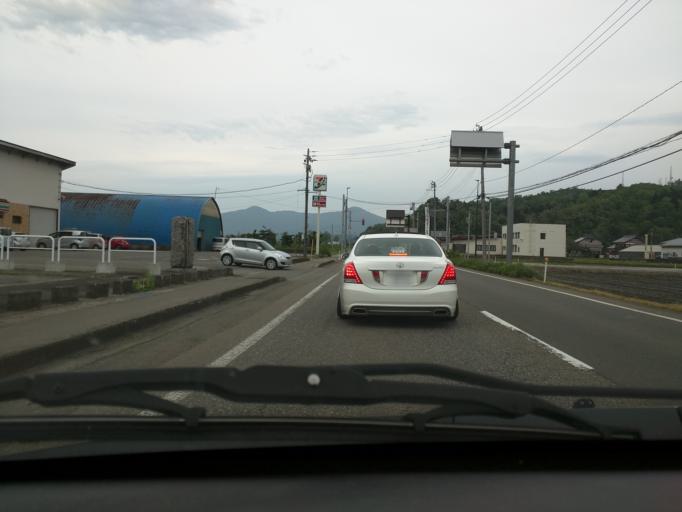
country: JP
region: Niigata
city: Muikamachi
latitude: 37.1935
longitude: 138.9462
